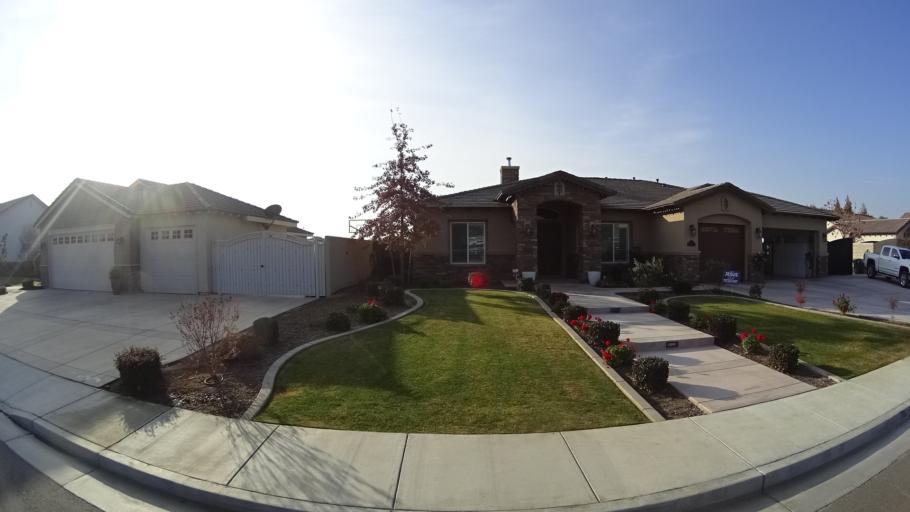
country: US
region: California
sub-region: Kern County
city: Rosedale
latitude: 35.3720
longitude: -119.1295
